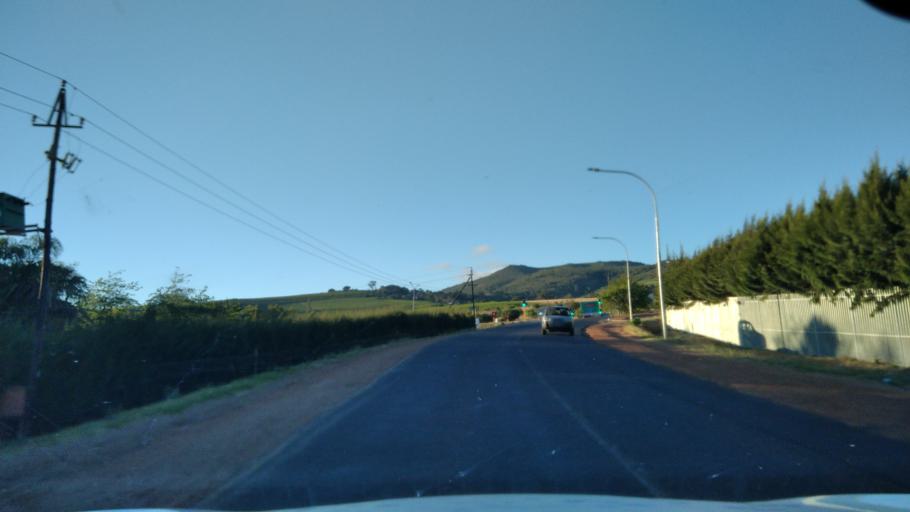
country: ZA
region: Western Cape
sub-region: Cape Winelands District Municipality
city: Paarl
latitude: -33.7844
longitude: 18.9518
